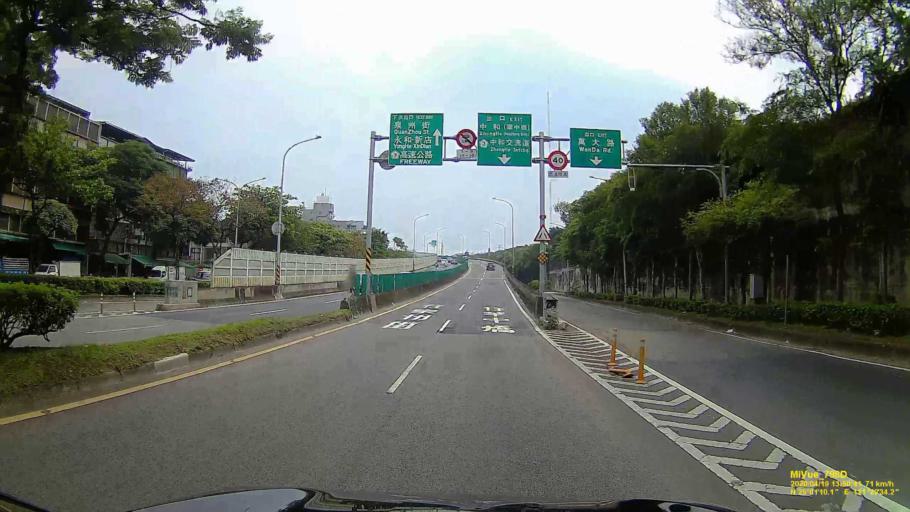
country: TW
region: Taipei
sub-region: Taipei
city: Banqiao
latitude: 25.0191
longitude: 121.4930
